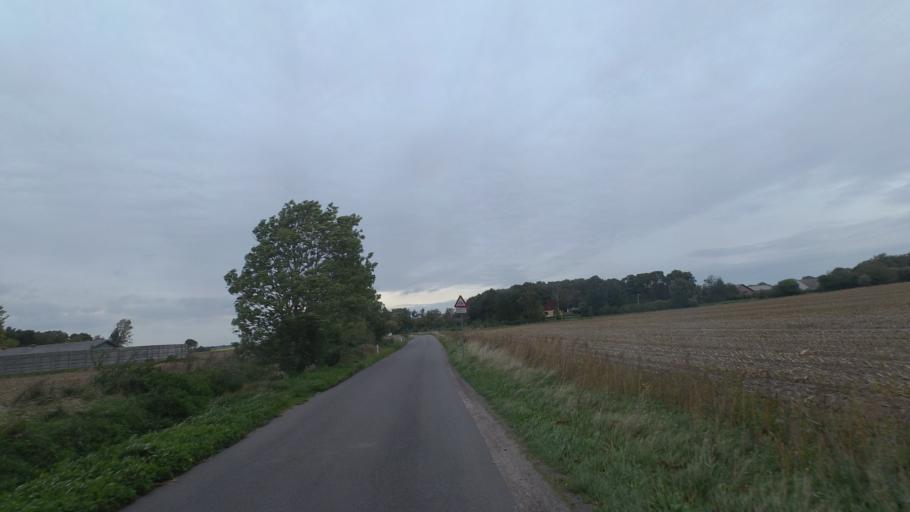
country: DK
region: Capital Region
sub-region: Bornholm Kommune
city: Akirkeby
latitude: 55.0079
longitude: 14.9916
